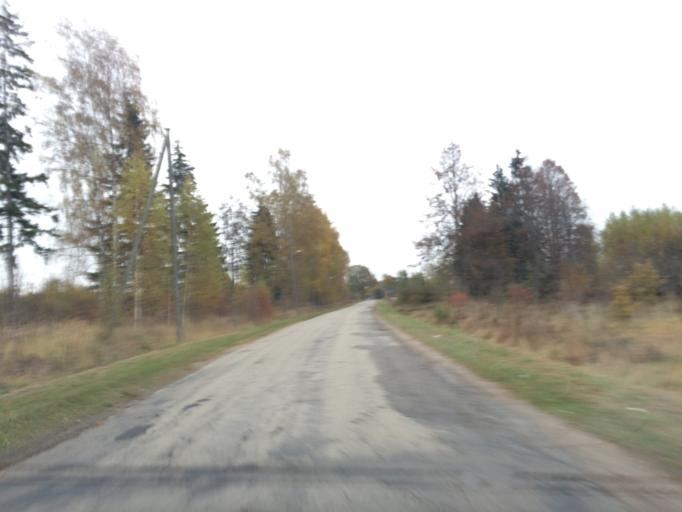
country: LV
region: Plavinu
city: Plavinas
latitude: 56.6157
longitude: 25.7654
